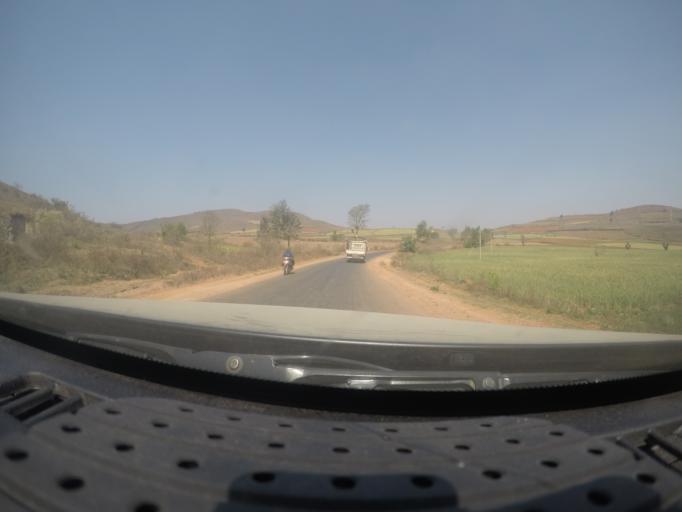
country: MM
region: Shan
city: Taunggyi
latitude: 20.8232
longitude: 96.6073
